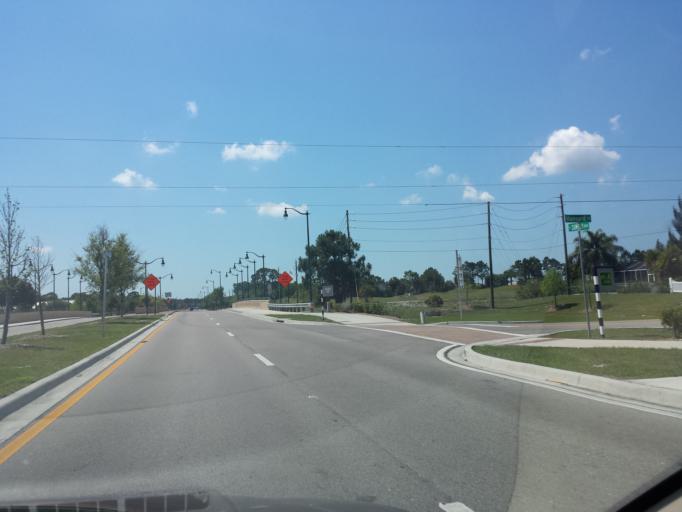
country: US
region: Florida
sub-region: Sarasota County
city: North Port
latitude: 27.0776
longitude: -82.2090
